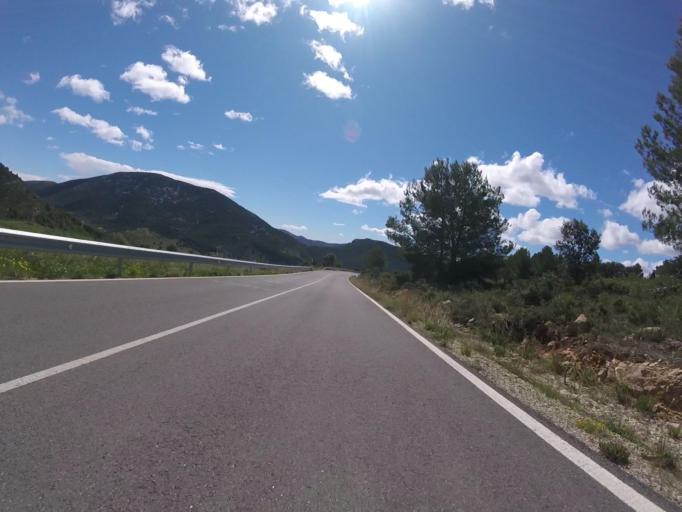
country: ES
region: Valencia
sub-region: Provincia de Castello
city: Culla
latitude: 40.2972
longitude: -0.1187
